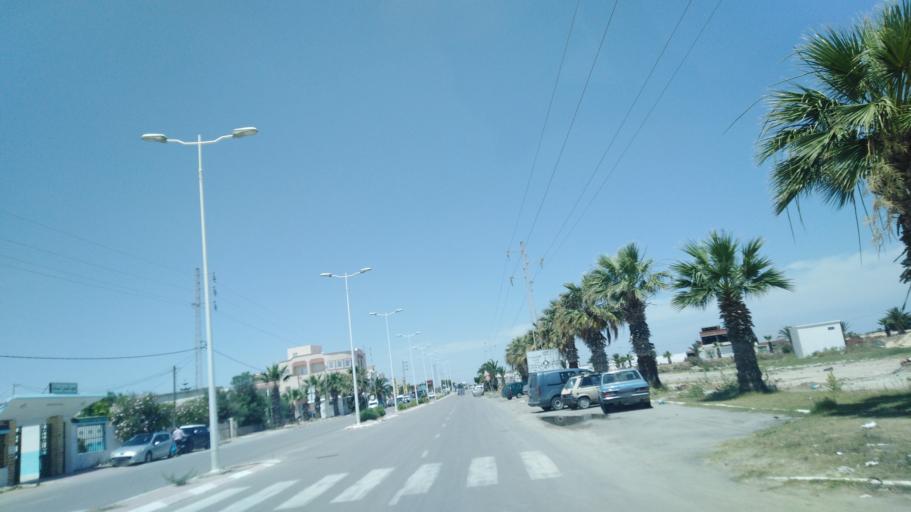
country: TN
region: Al Mahdiyah
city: Ksour Essaf
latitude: 35.4249
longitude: 10.9952
